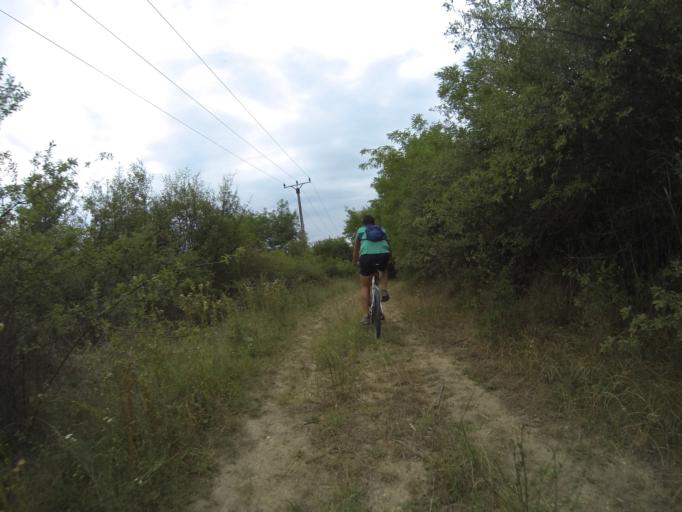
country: RO
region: Dolj
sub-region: Comuna Almaju
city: Almaju
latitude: 44.4737
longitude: 23.6936
